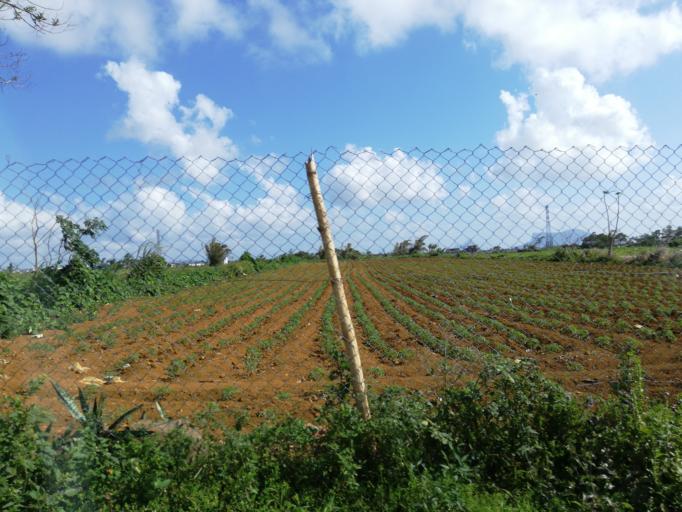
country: MU
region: Pamplemousses
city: Creve Coeur
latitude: -20.2069
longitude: 57.5488
